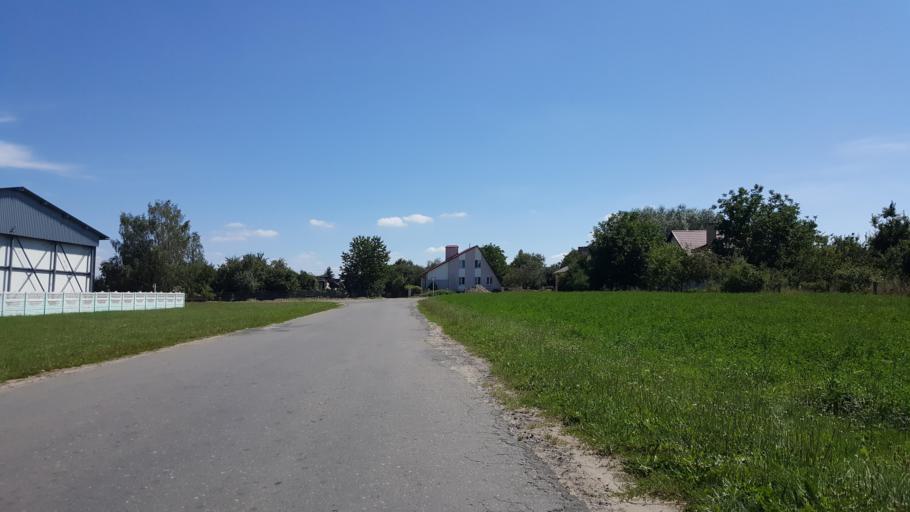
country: BY
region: Brest
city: Charnawchytsy
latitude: 52.2697
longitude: 23.5858
